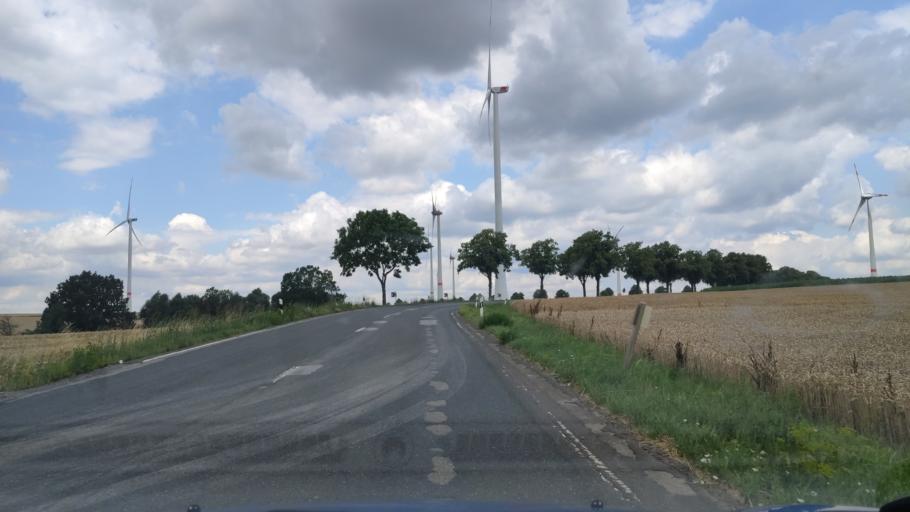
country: DE
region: Lower Saxony
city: Coppenbrugge
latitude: 52.1189
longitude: 9.5038
